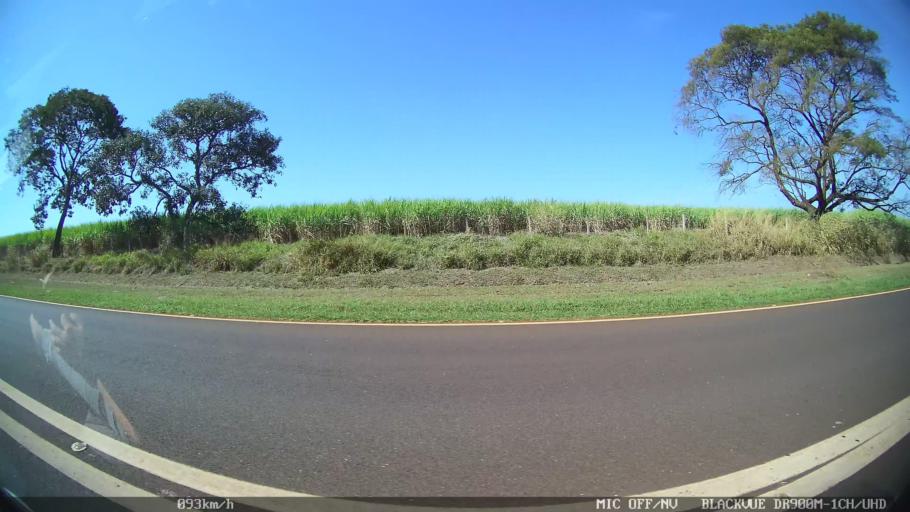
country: BR
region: Sao Paulo
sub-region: Batatais
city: Batatais
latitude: -20.8315
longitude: -47.5992
